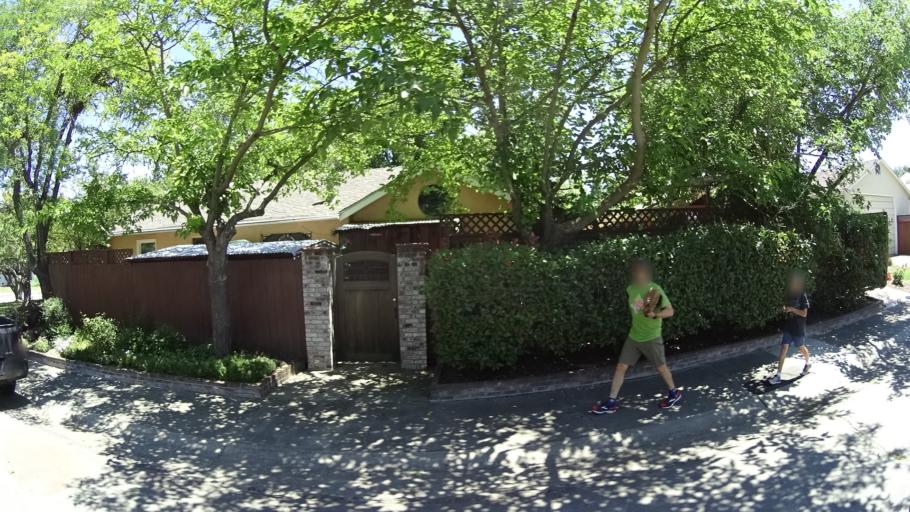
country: US
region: California
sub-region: Sacramento County
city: Sacramento
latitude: 38.5770
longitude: -121.4398
